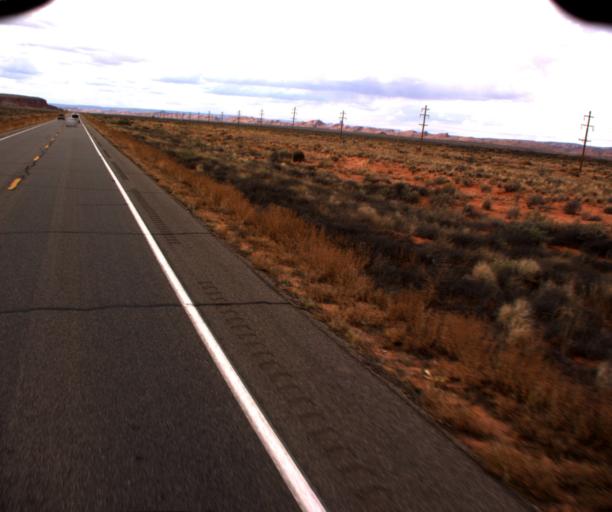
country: US
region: Arizona
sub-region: Navajo County
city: Kayenta
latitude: 36.7862
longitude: -109.9614
